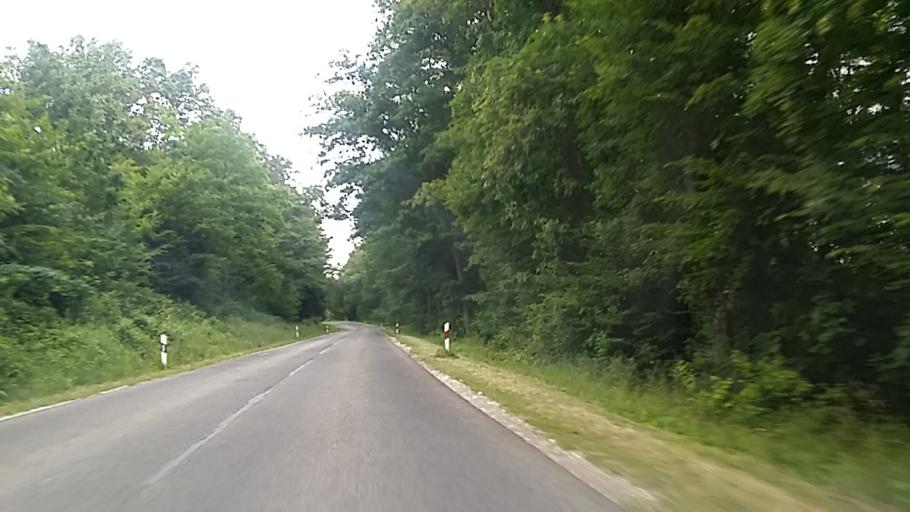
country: SI
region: Hodos-Hodos
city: Hodos
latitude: 46.8328
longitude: 16.4426
